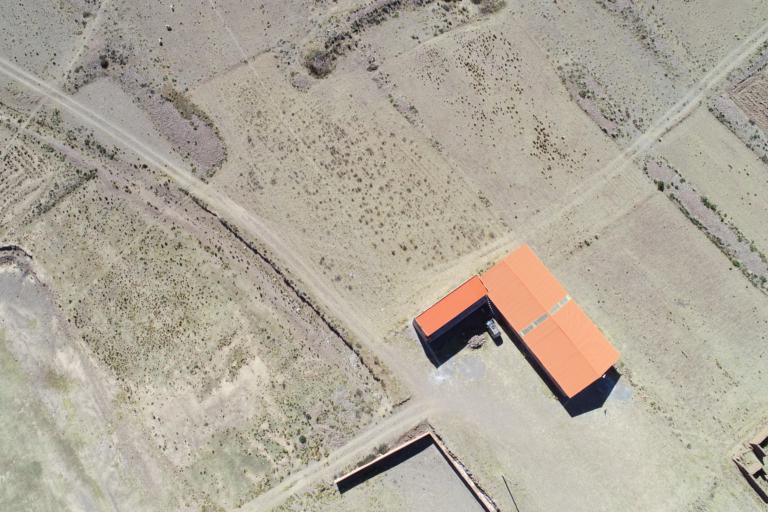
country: BO
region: La Paz
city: Achacachi
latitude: -15.8970
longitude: -68.9011
